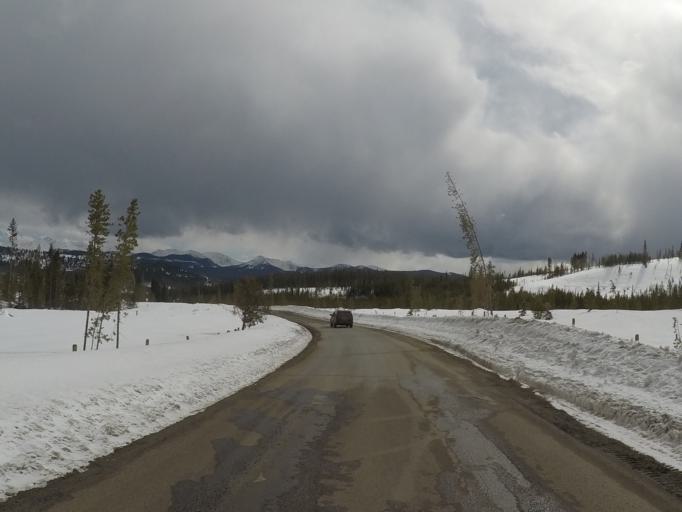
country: US
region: Montana
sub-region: Granite County
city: Philipsburg
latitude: 46.2165
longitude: -113.2574
